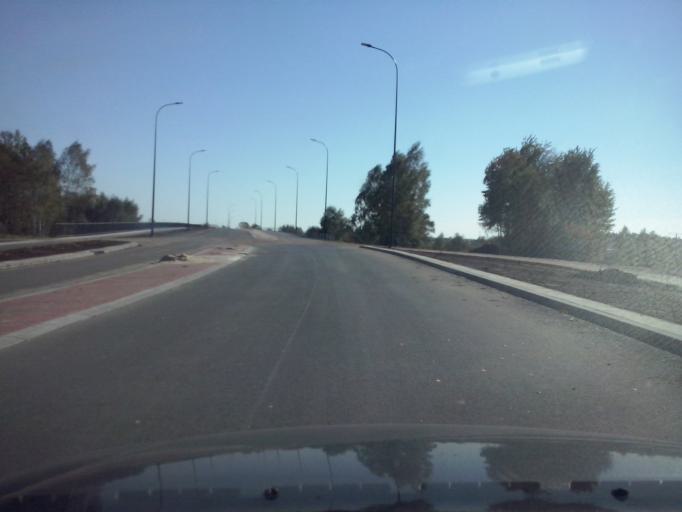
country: PL
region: Lublin Voivodeship
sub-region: Powiat bilgorajski
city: Bilgoraj
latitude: 50.5225
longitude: 22.7090
